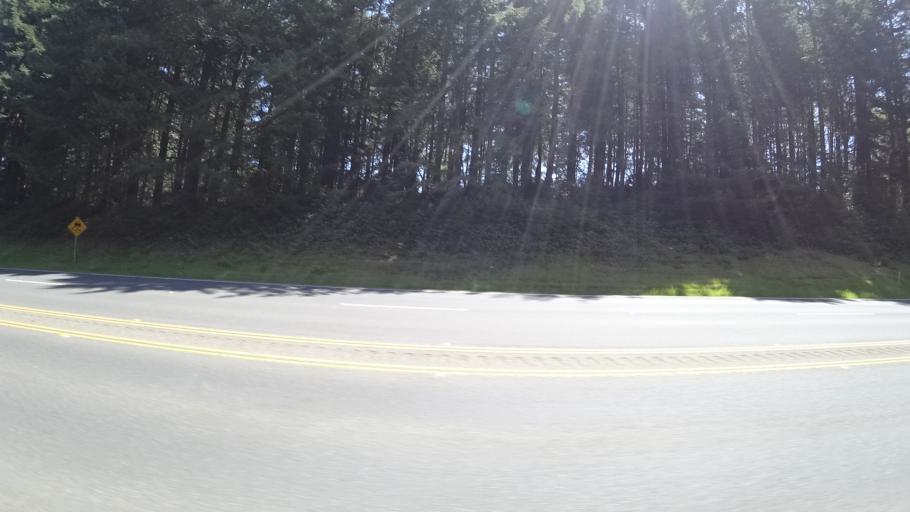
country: US
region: California
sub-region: Humboldt County
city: Westhaven-Moonstone
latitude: 41.1429
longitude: -124.1365
